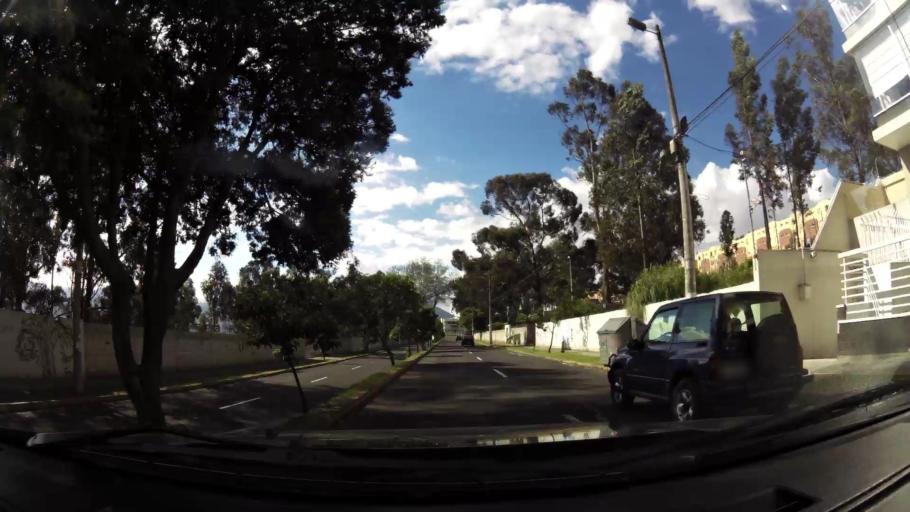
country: EC
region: Pichincha
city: Quito
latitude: -0.1093
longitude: -78.4822
